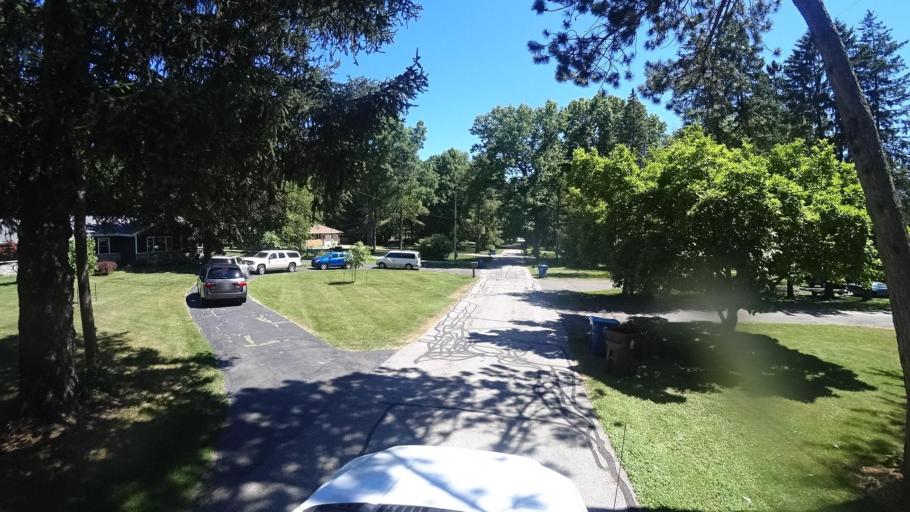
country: US
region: Indiana
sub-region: Porter County
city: Porter
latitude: 41.6249
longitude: -87.0807
